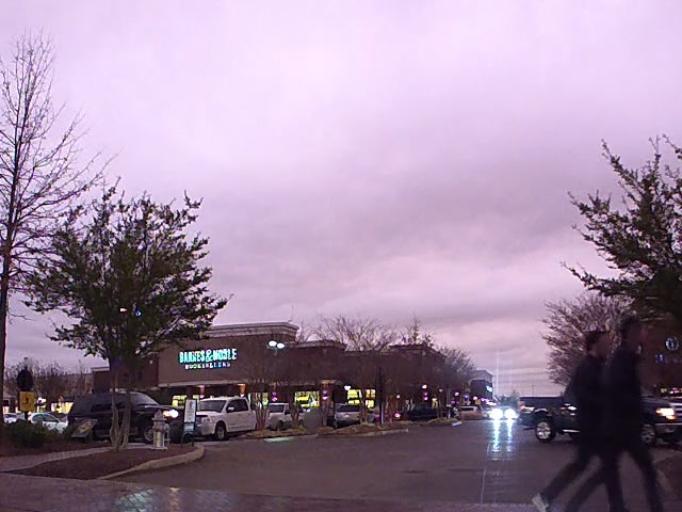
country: US
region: Tennessee
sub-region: Shelby County
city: Collierville
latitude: 35.0242
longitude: -89.7197
